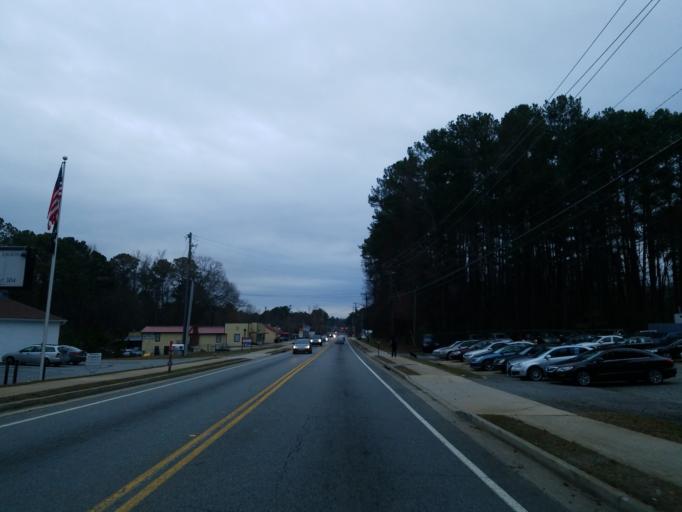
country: US
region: Georgia
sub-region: Cobb County
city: Acworth
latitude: 34.0576
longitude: -84.6643
